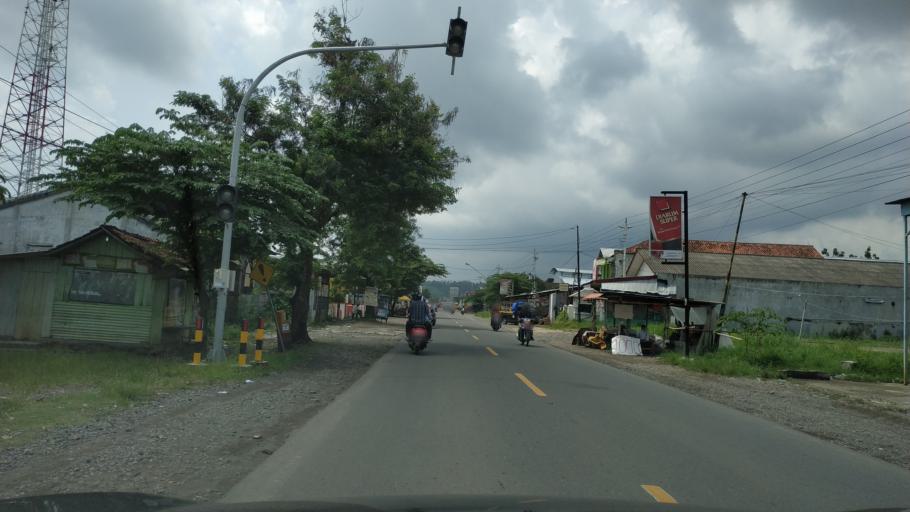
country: ID
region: Central Java
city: Lebaksiu
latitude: -7.0462
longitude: 109.1394
